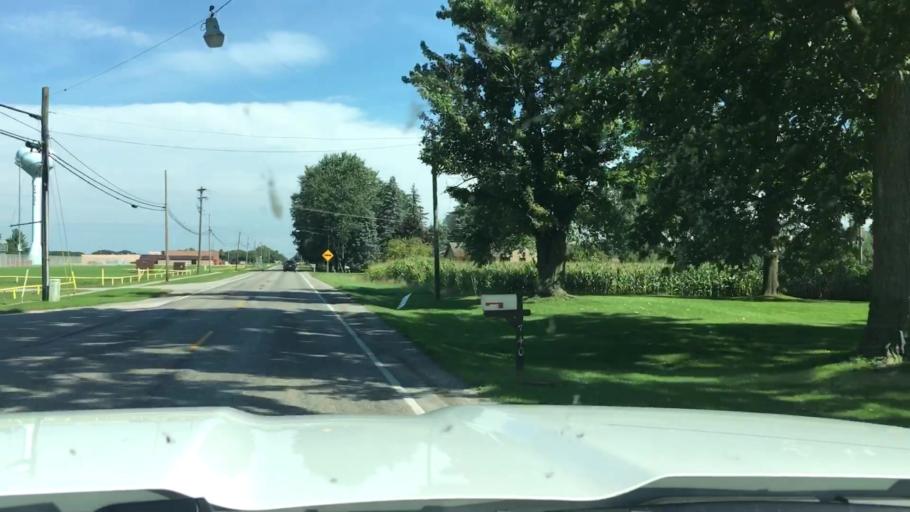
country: US
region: Michigan
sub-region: Saginaw County
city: Hemlock
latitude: 43.4195
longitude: -84.2298
